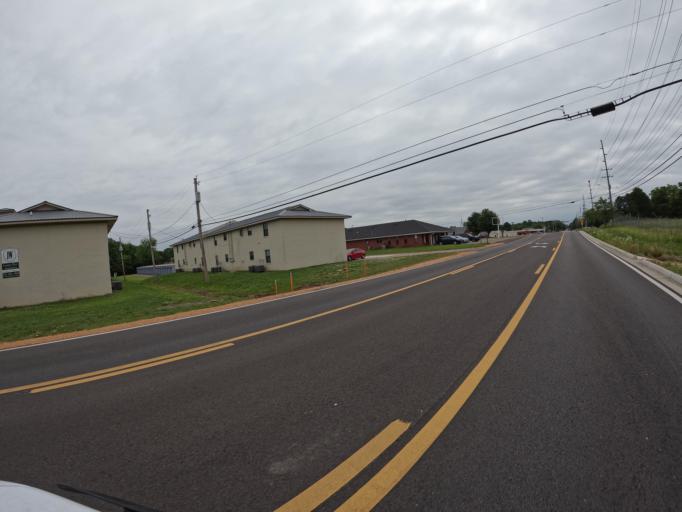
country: US
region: Mississippi
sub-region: Lee County
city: Tupelo
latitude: 34.2647
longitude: -88.7598
